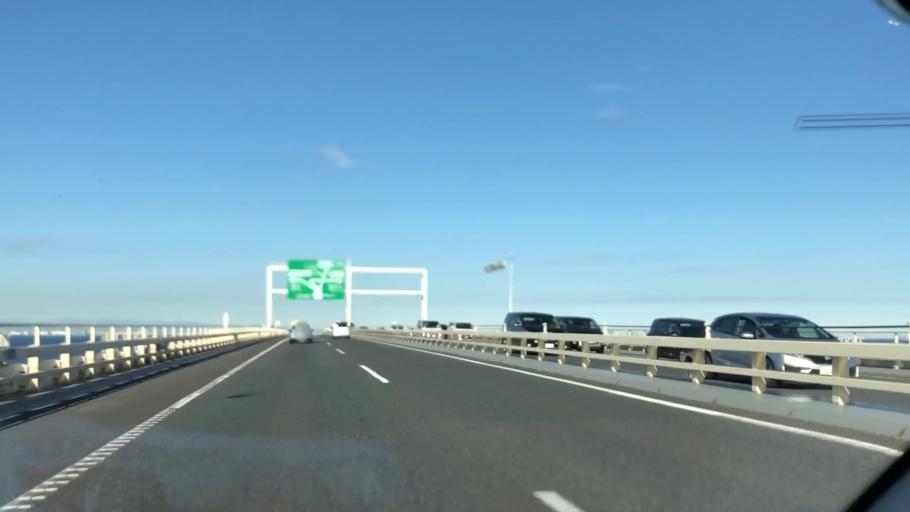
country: JP
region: Chiba
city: Kisarazu
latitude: 35.4547
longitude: 139.8884
